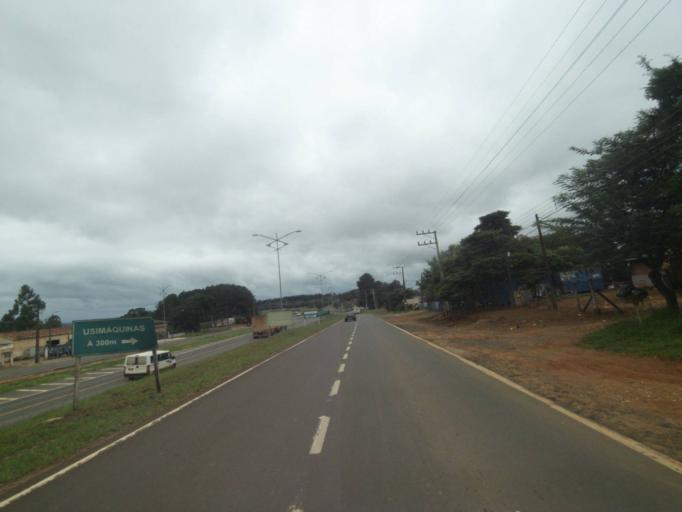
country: BR
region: Parana
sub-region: Telemaco Borba
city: Telemaco Borba
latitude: -24.3454
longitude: -50.6592
